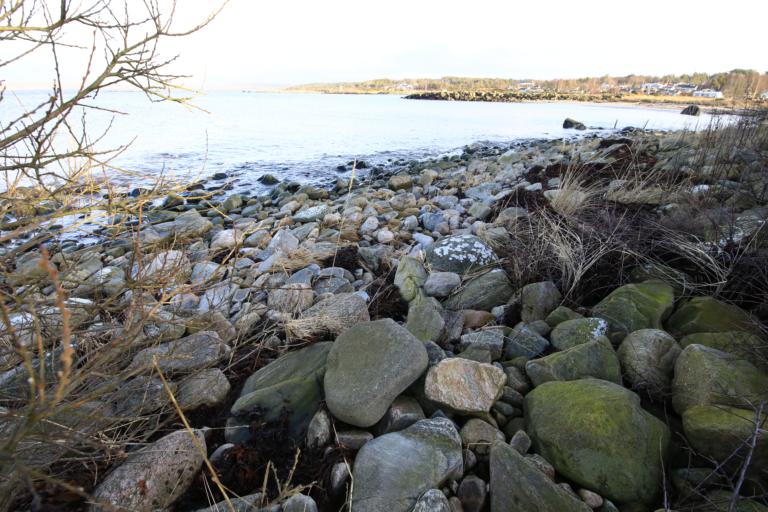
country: SE
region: Halland
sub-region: Kungsbacka Kommun
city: Frillesas
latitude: 57.2003
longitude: 12.1699
